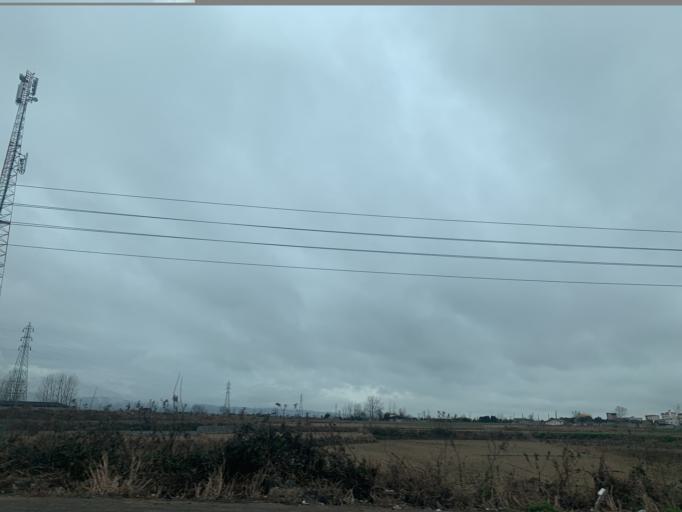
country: IR
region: Mazandaran
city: Amol
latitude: 36.4233
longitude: 52.3497
